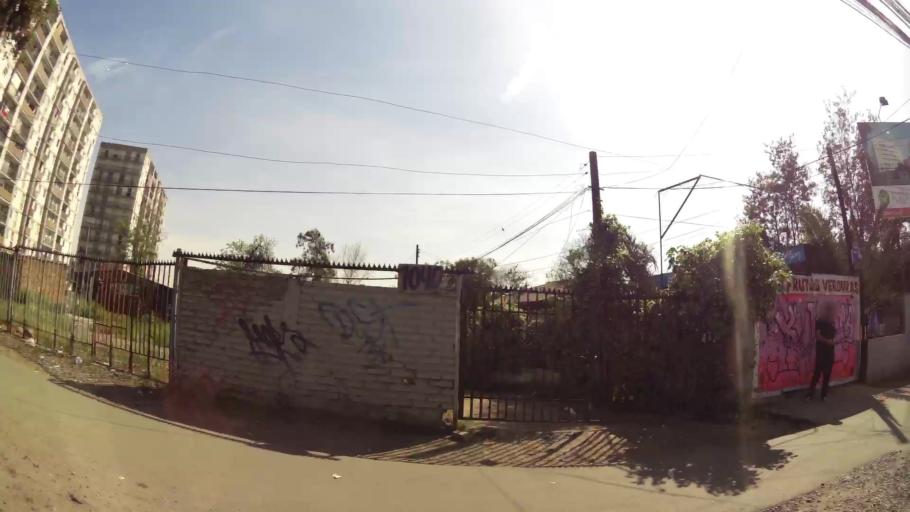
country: CL
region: Santiago Metropolitan
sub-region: Provincia de Santiago
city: Villa Presidente Frei, Nunoa, Santiago, Chile
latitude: -33.5226
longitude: -70.5867
